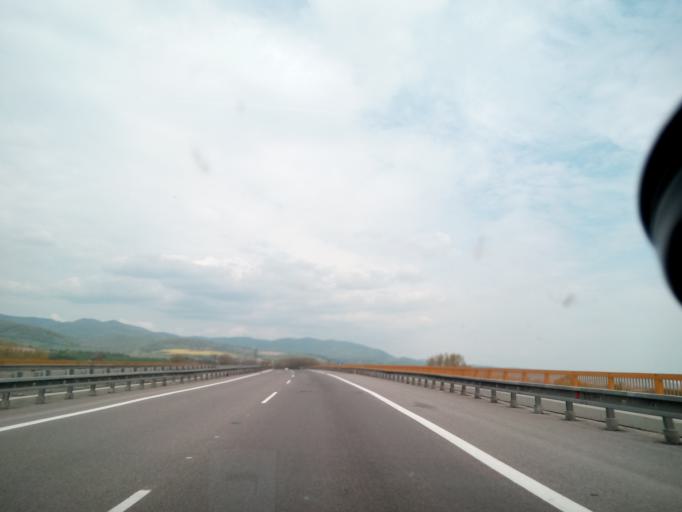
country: SK
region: Trenciansky
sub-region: Okres Nove Mesto nad Vahom
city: Nove Mesto nad Vahom
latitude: 48.8095
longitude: 17.9064
